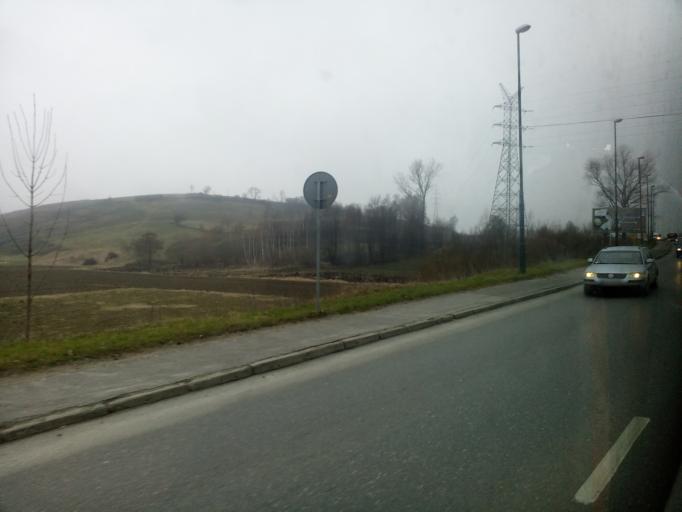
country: PL
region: Lesser Poland Voivodeship
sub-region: Powiat nowosadecki
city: Stary Sacz
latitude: 49.5743
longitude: 20.6631
